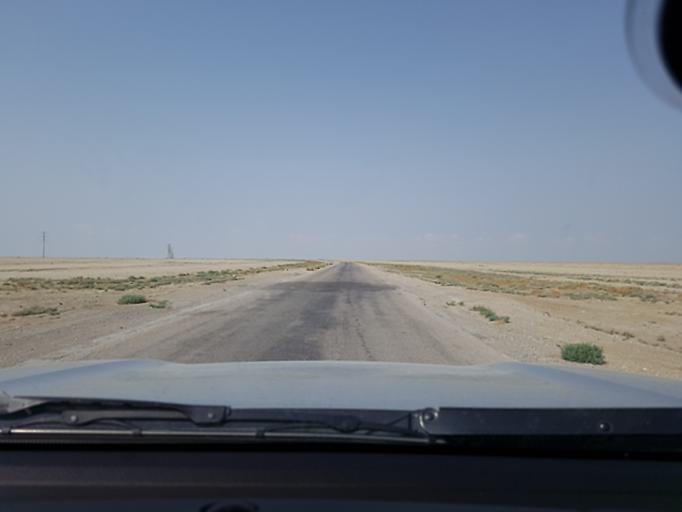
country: TM
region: Balkan
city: Gumdag
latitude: 38.7172
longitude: 54.4671
